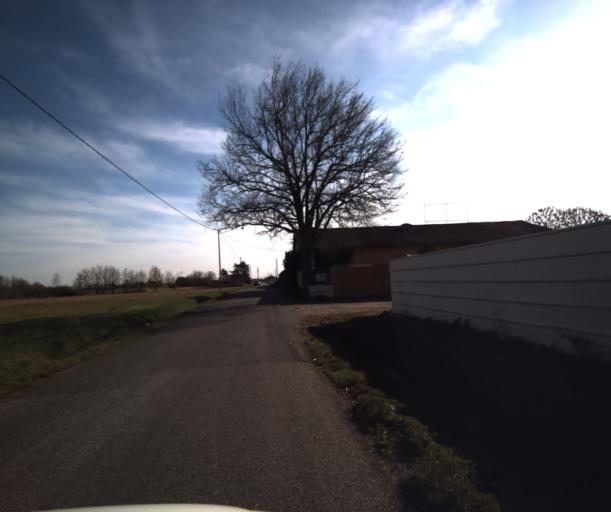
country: FR
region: Midi-Pyrenees
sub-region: Departement du Tarn-et-Garonne
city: Labastide-Saint-Pierre
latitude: 43.9320
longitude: 1.3419
